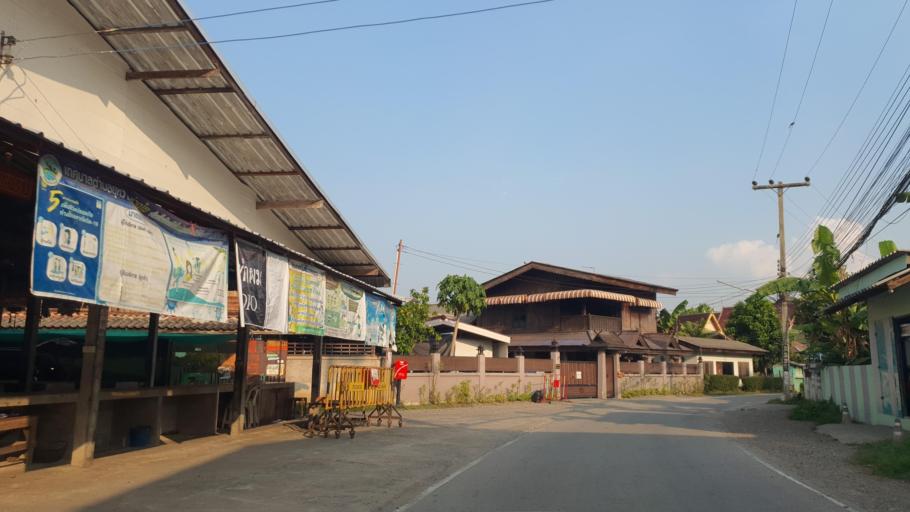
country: TH
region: Chiang Mai
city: San Pa Tong
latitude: 18.6372
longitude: 98.8621
